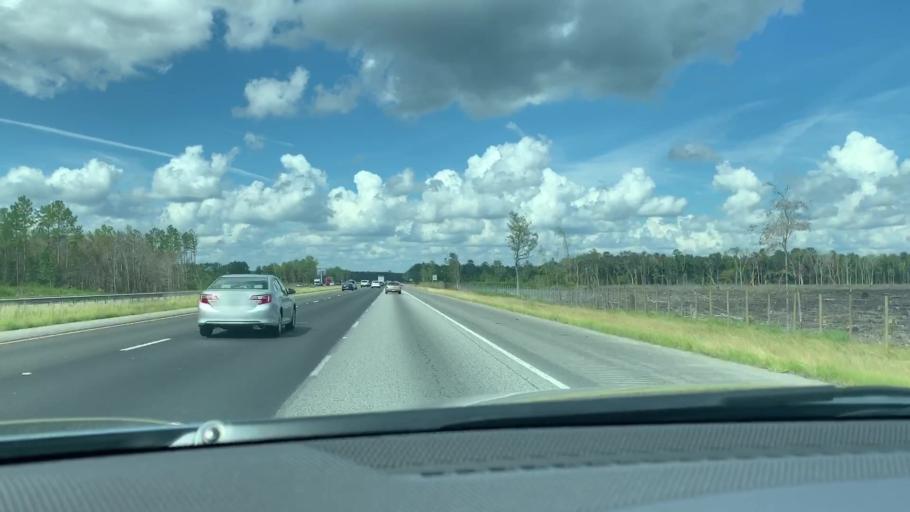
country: US
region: Georgia
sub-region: Camden County
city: Kingsland
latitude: 30.8593
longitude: -81.6781
